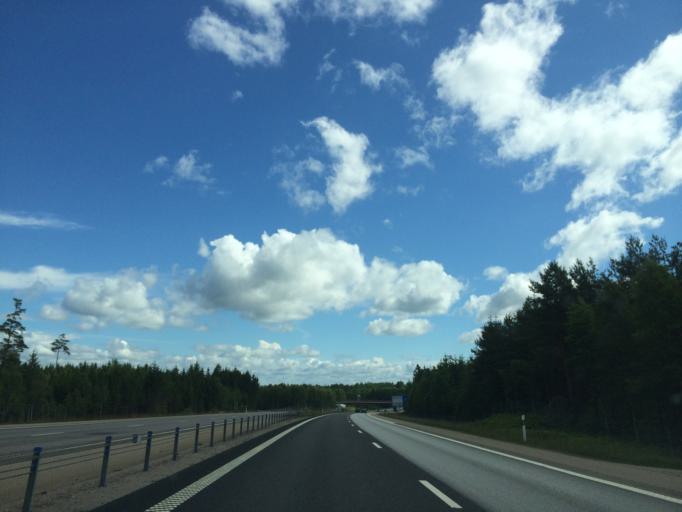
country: SE
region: Kronoberg
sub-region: Markaryds Kommun
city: Stromsnasbruk
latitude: 56.6132
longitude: 13.7550
